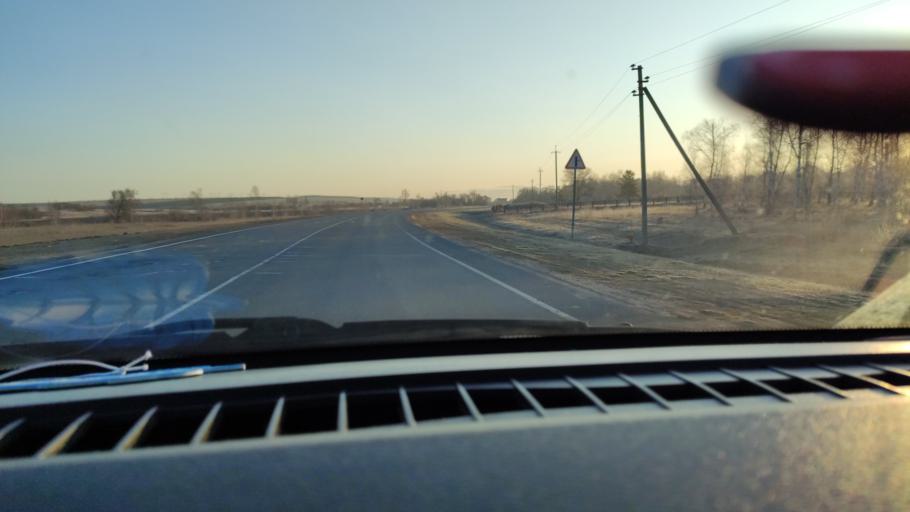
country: RU
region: Saratov
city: Sinodskoye
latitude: 52.0401
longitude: 46.7331
